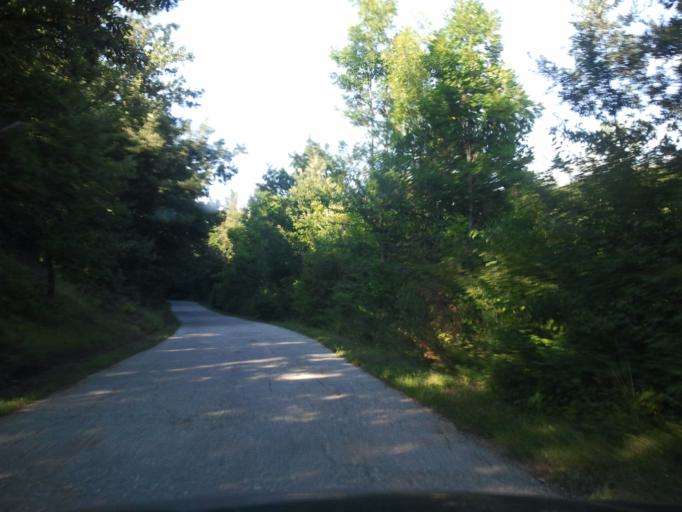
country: HR
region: Zadarska
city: Obrovac
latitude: 44.3353
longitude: 15.6429
